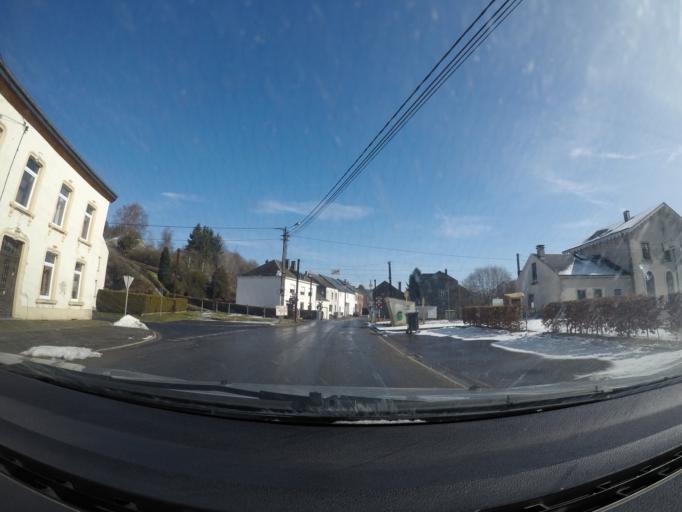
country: BE
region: Wallonia
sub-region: Province du Luxembourg
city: Leglise
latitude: 49.7660
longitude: 5.5175
